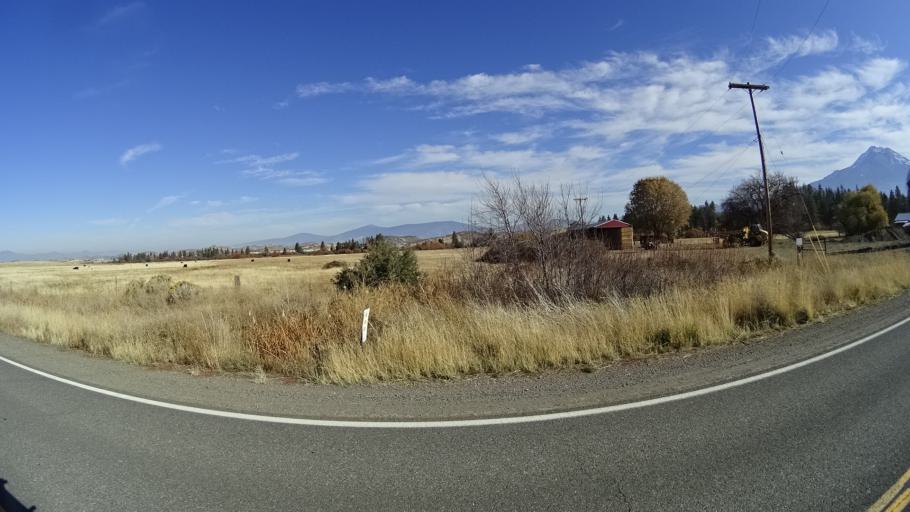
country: US
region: California
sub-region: Siskiyou County
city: Weed
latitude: 41.4500
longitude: -122.4534
